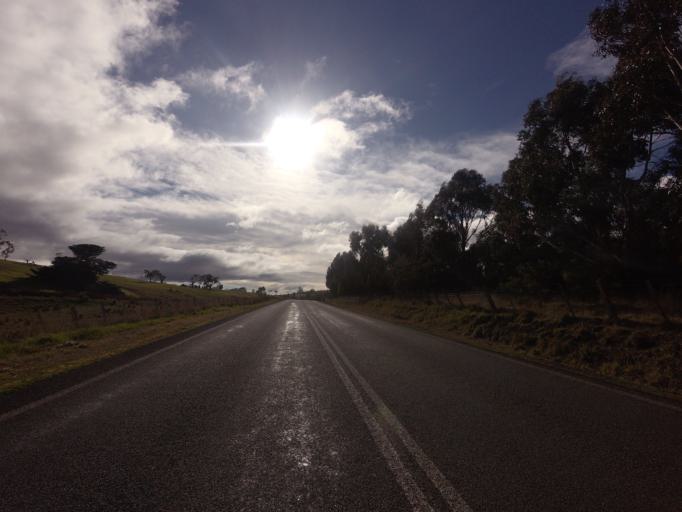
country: AU
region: Tasmania
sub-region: Derwent Valley
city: New Norfolk
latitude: -42.6051
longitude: 146.8853
